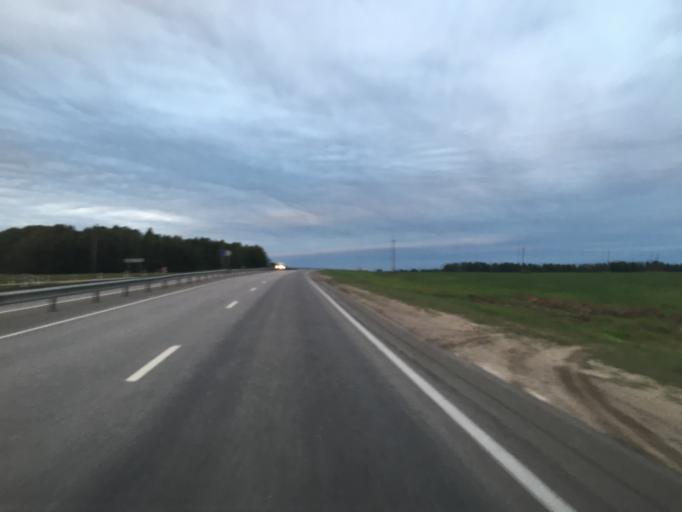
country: RU
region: Kaluga
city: Kaluga
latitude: 54.6656
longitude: 36.2855
